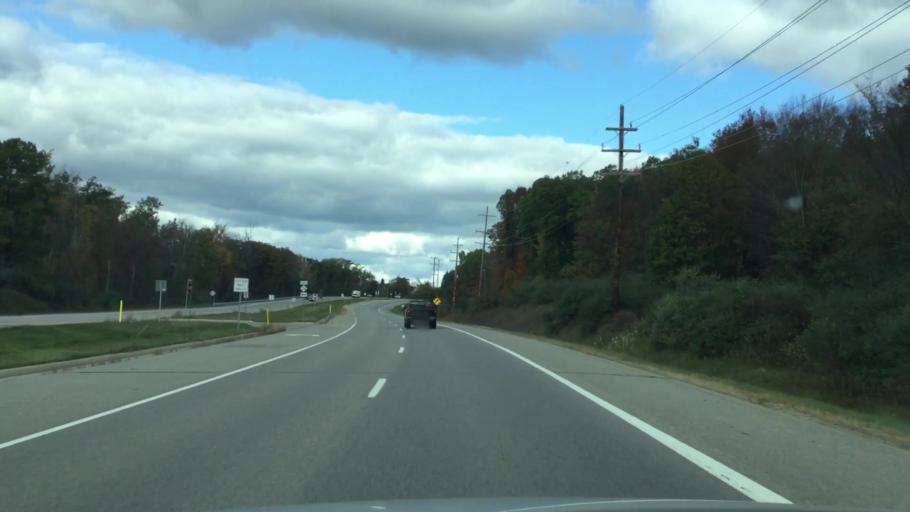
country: US
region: Michigan
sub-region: Lapeer County
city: Lapeer
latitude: 42.9913
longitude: -83.3169
